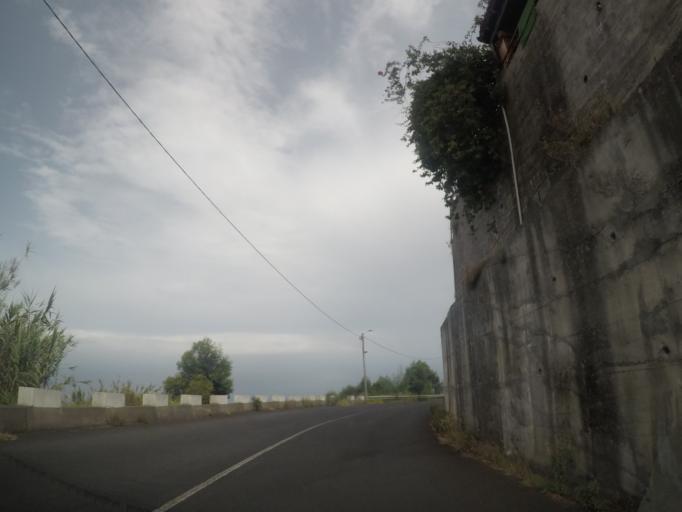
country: PT
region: Madeira
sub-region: Santa Cruz
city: Santa Cruz
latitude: 32.6754
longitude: -16.8190
